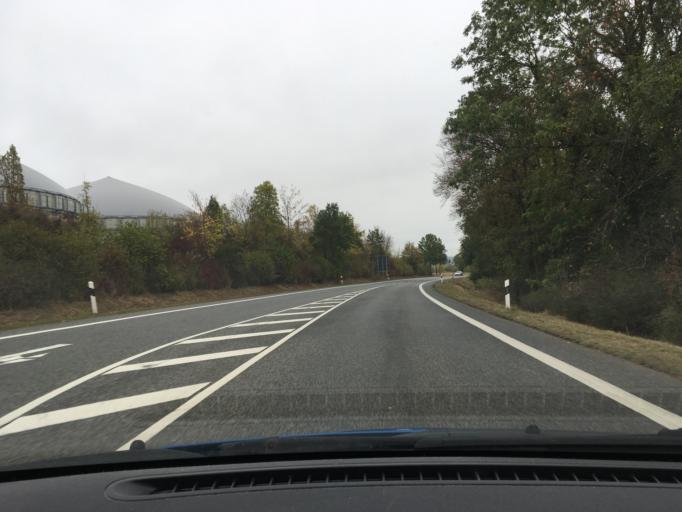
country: DE
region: Lower Saxony
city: Hardegsen
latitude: 51.6446
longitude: 9.8607
